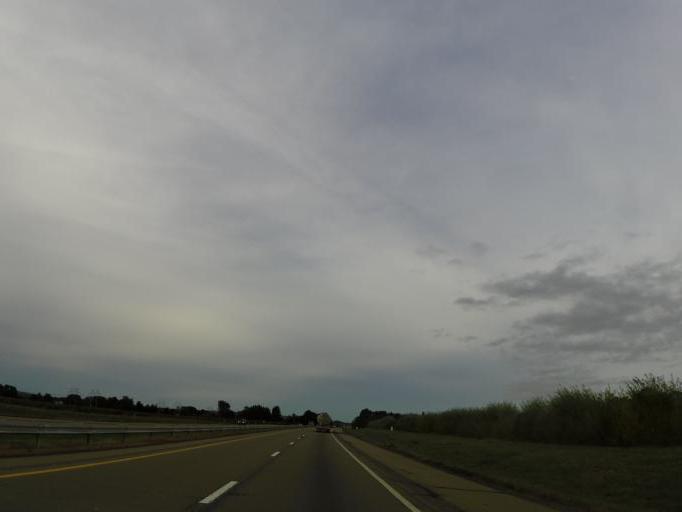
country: US
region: New York
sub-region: Chautauqua County
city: Silver Creek
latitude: 42.5287
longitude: -79.1358
